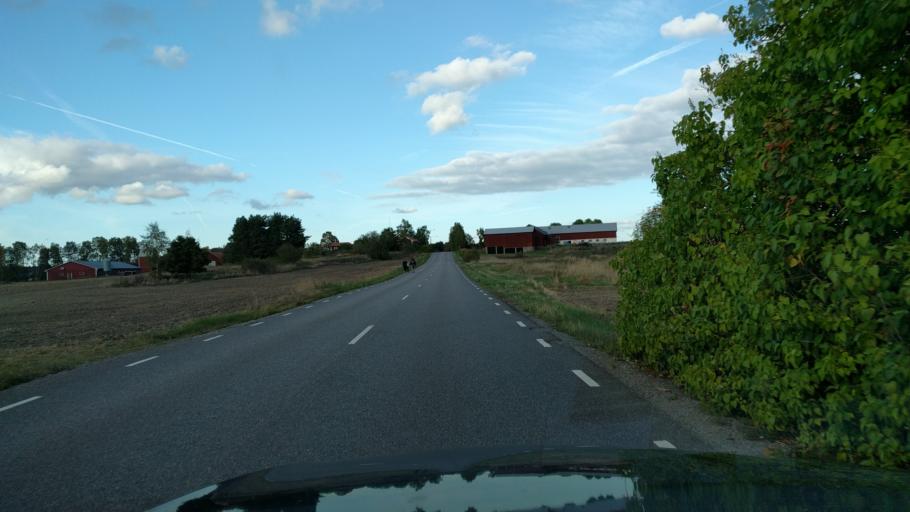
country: SE
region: Uppsala
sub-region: Osthammars Kommun
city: Bjorklinge
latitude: 60.1502
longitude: 17.5849
